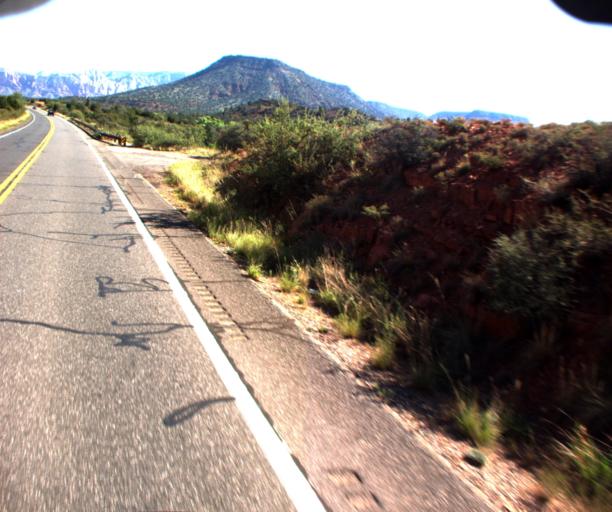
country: US
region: Arizona
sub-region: Yavapai County
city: Big Park
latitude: 34.7466
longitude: -111.7672
